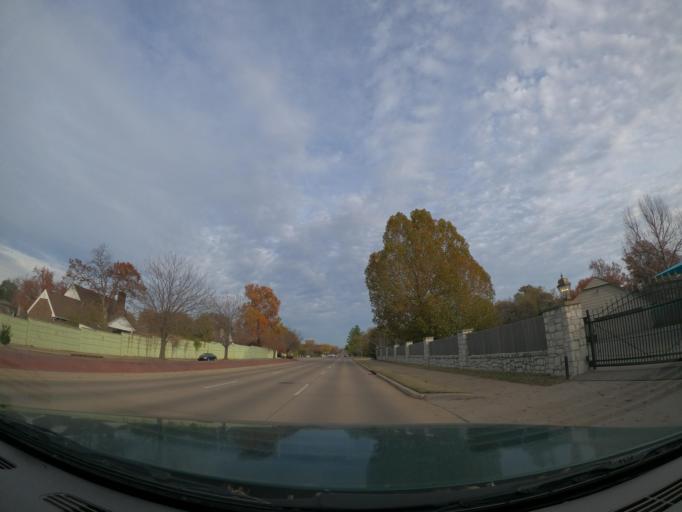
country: US
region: Oklahoma
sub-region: Tulsa County
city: Jenks
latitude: 36.0608
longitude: -95.9364
